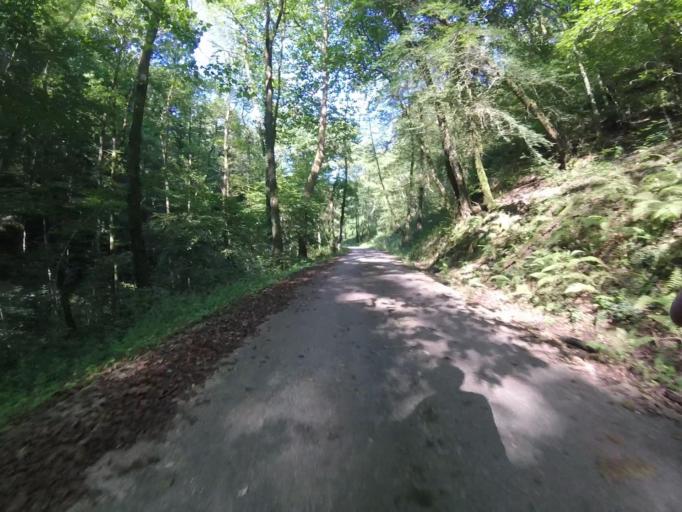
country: ES
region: Basque Country
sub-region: Provincia de Guipuzcoa
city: Astigarraga
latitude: 43.2419
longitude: -1.9239
